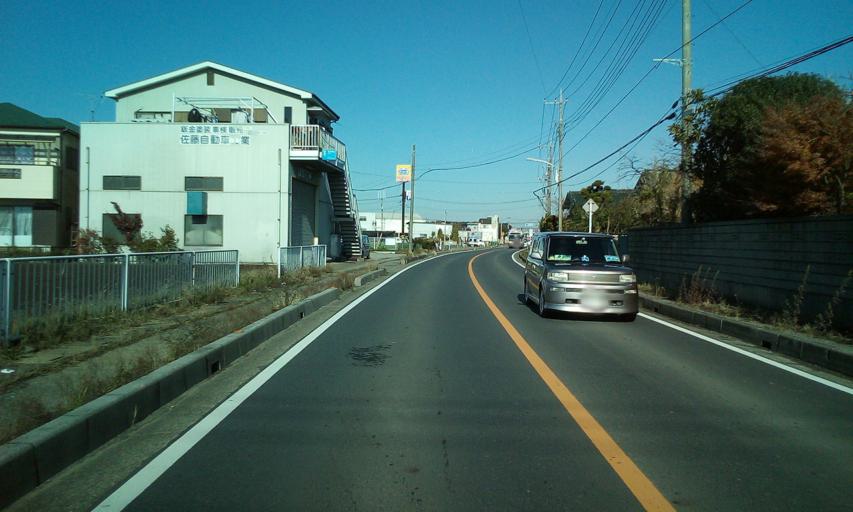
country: JP
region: Chiba
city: Nagareyama
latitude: 35.8649
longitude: 139.8883
